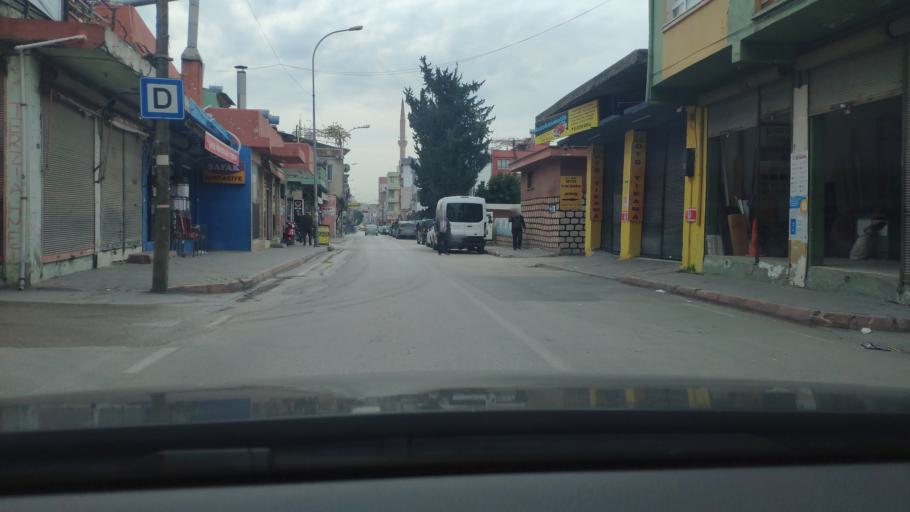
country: TR
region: Adana
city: Adana
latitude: 37.0168
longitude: 35.3144
